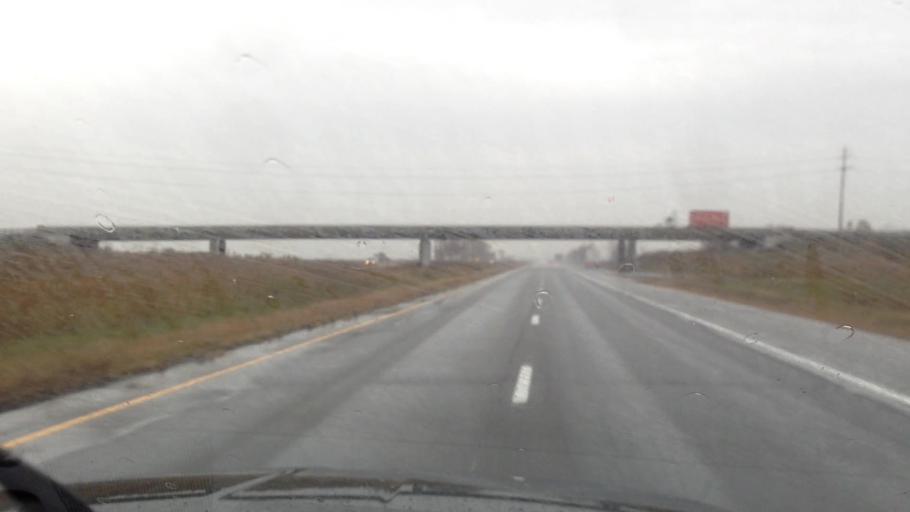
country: CA
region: Ontario
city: Casselman
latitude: 45.3256
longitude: -74.9869
